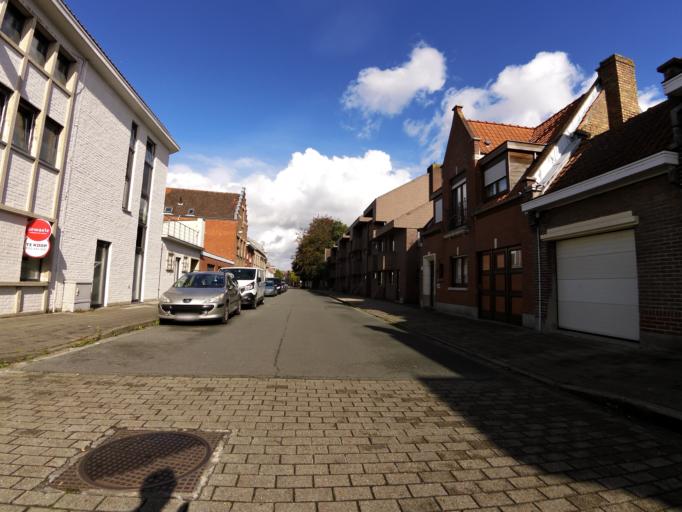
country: BE
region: Flanders
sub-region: Provincie West-Vlaanderen
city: Brugge
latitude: 51.1996
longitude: 3.1999
